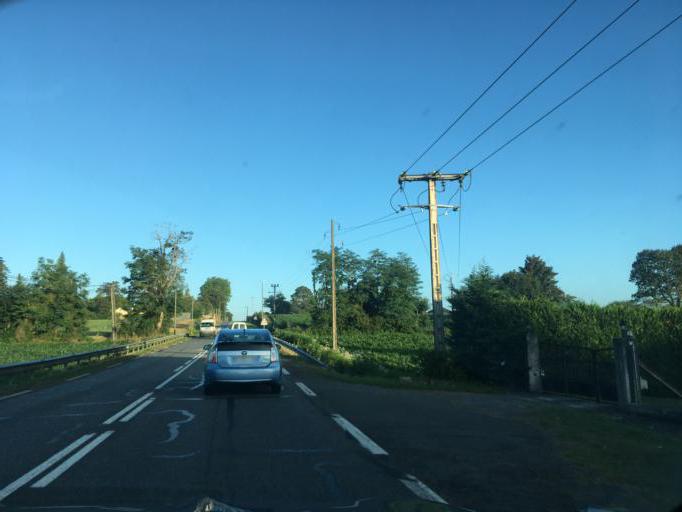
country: FR
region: Aquitaine
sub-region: Departement des Pyrenees-Atlantiques
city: Ger
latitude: 43.2459
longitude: -0.0353
